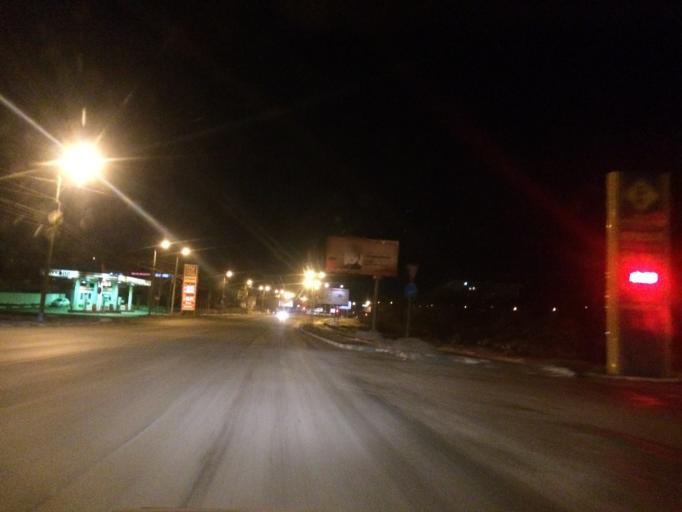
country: RU
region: Tula
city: Mendeleyevskiy
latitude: 54.1567
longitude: 37.6001
